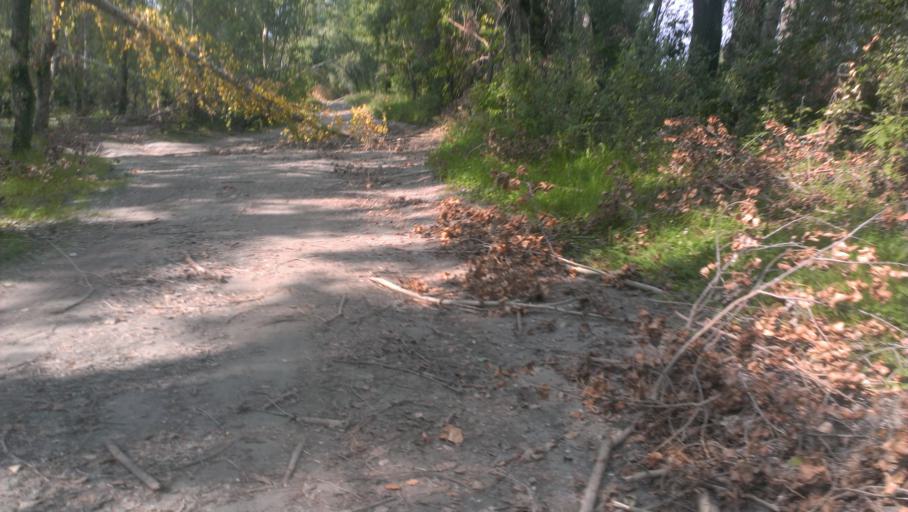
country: RU
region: Altai Krai
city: Novoaltaysk
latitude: 53.3719
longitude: 83.8568
